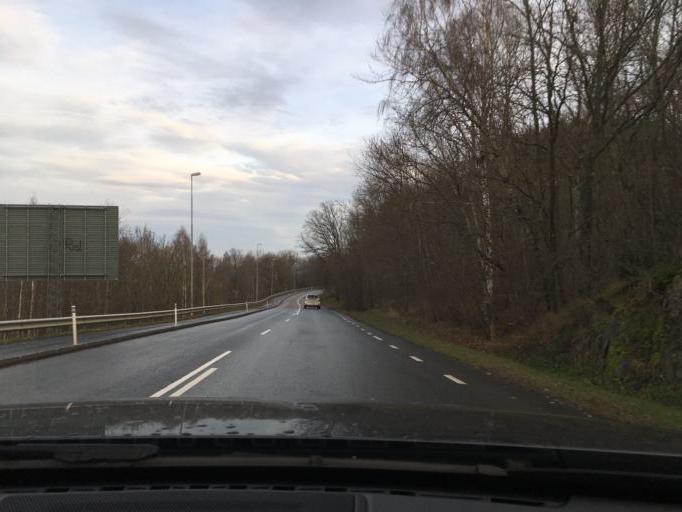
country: SE
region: Joenkoeping
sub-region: Jonkopings Kommun
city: Graenna
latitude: 58.0041
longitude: 14.4523
